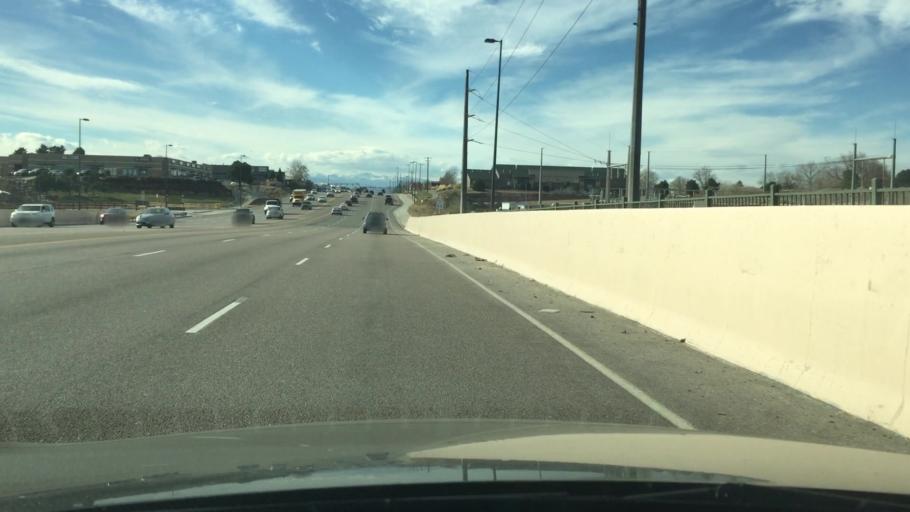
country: US
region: Colorado
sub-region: Arapahoe County
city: Dove Valley
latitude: 39.5951
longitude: -104.8138
